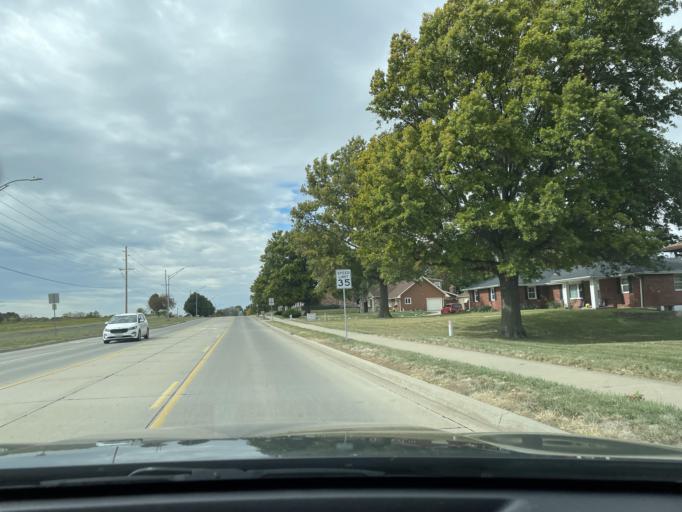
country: US
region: Missouri
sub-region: Buchanan County
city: Saint Joseph
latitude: 39.7699
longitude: -94.7813
